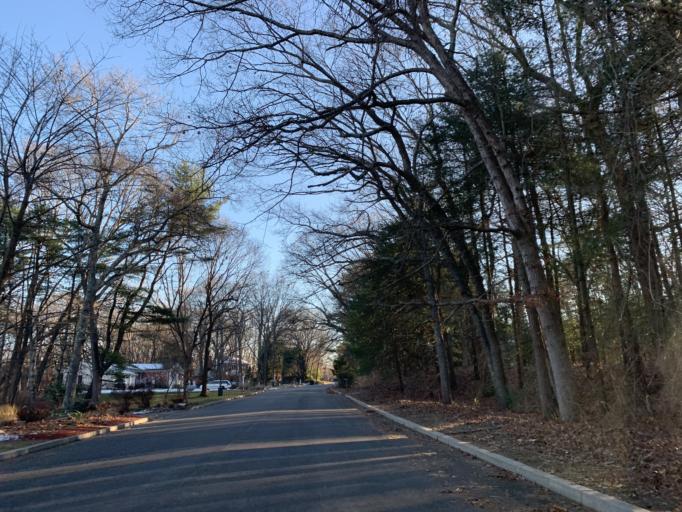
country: US
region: Rhode Island
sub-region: Washington County
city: Exeter
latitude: 41.6274
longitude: -71.5186
